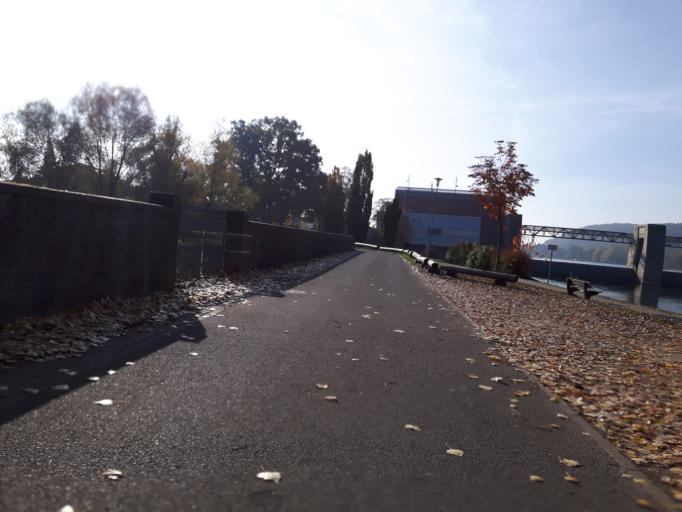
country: DE
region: Bavaria
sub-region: Regierungsbezirk Unterfranken
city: Kleinwallstadt
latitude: 49.8701
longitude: 9.1620
